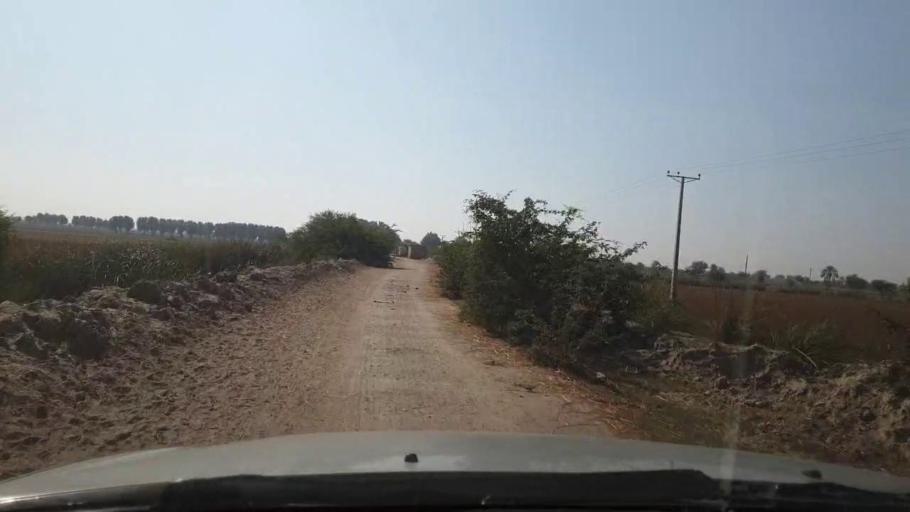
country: PK
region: Sindh
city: Kario
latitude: 24.8895
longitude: 68.5588
